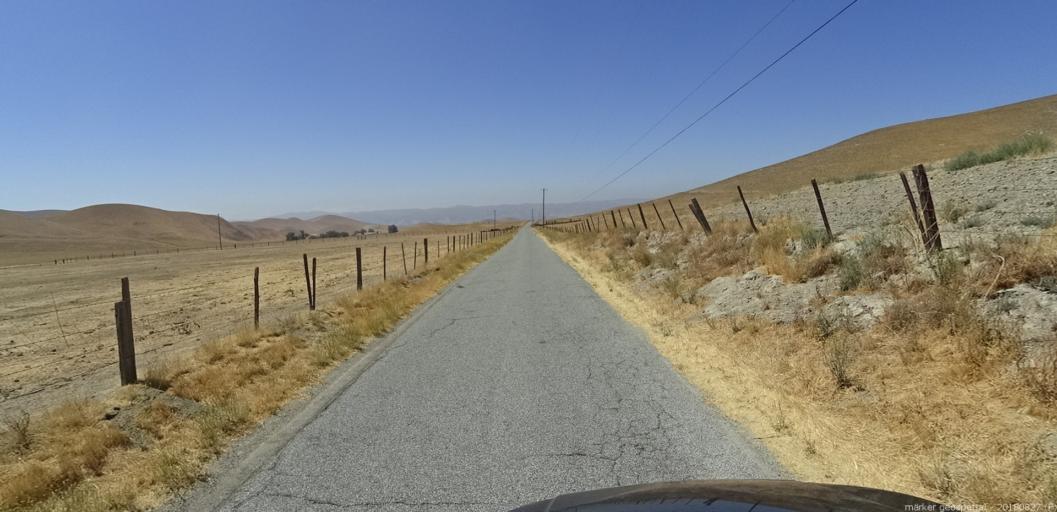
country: US
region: California
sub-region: Monterey County
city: King City
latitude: 36.0900
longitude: -120.8908
